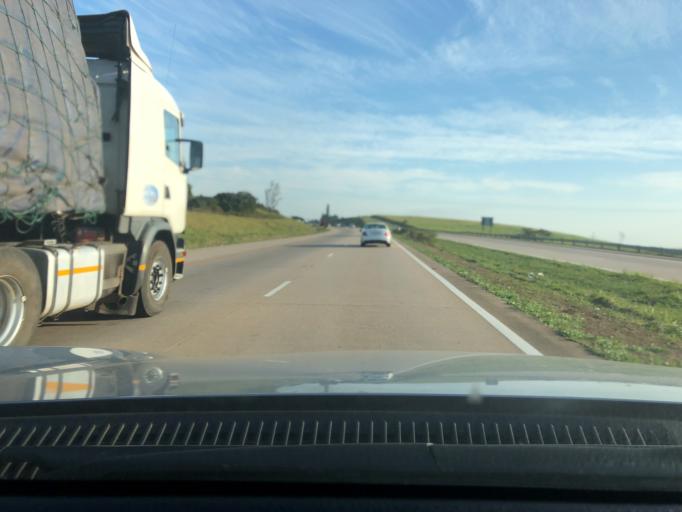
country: ZA
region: KwaZulu-Natal
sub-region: iLembe District Municipality
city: Stanger
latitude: -29.4182
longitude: 31.2756
